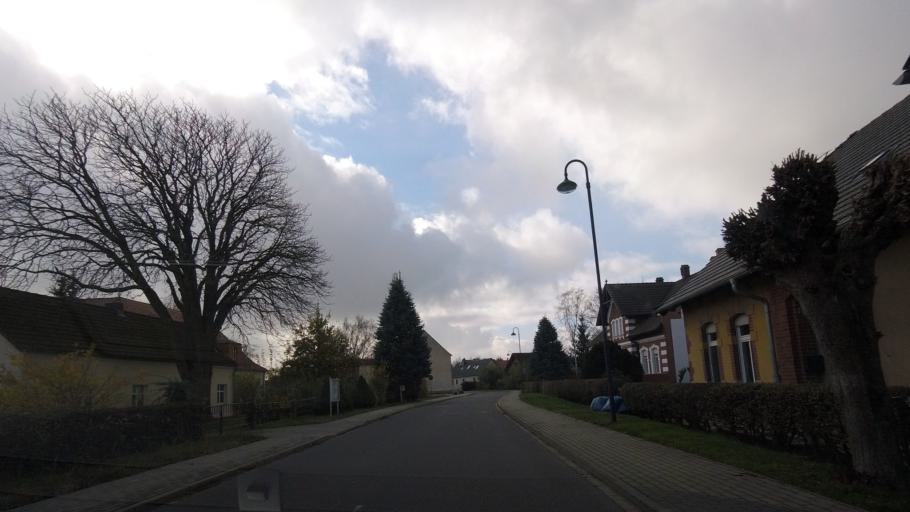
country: DE
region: Brandenburg
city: Niedergorsdorf
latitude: 52.0078
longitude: 12.9375
